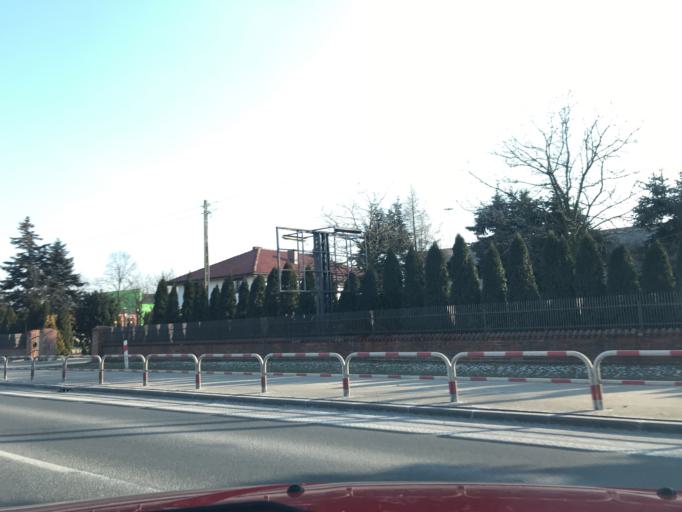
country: PL
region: Greater Poland Voivodeship
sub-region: Powiat pleszewski
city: Pleszew
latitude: 51.8936
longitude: 17.8191
